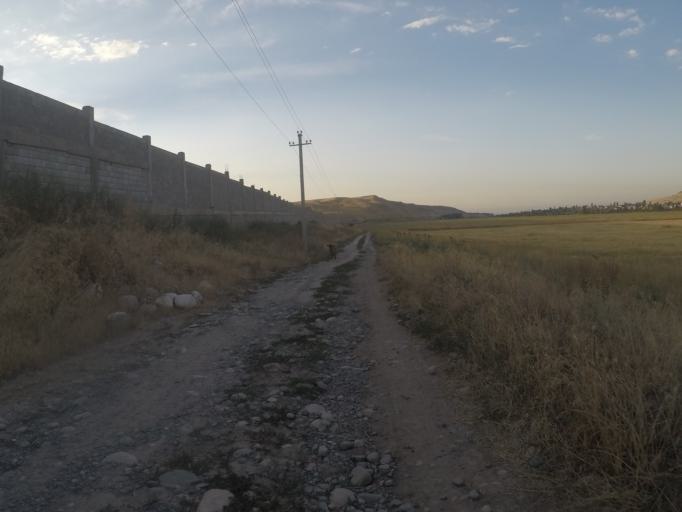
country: KG
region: Chuy
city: Bishkek
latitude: 42.7529
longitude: 74.6367
